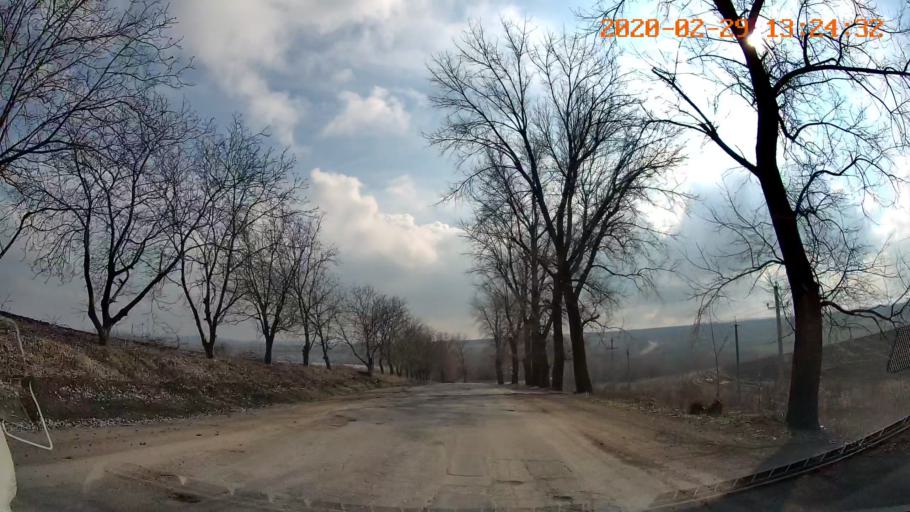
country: MD
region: Telenesti
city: Camenca
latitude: 47.9378
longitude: 28.6279
